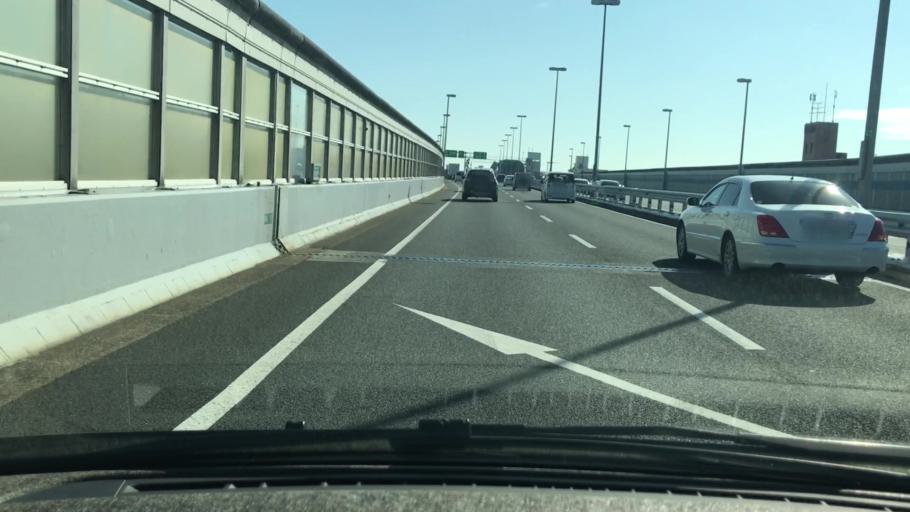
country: JP
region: Hyogo
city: Nishinomiya-hama
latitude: 34.7288
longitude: 135.3520
